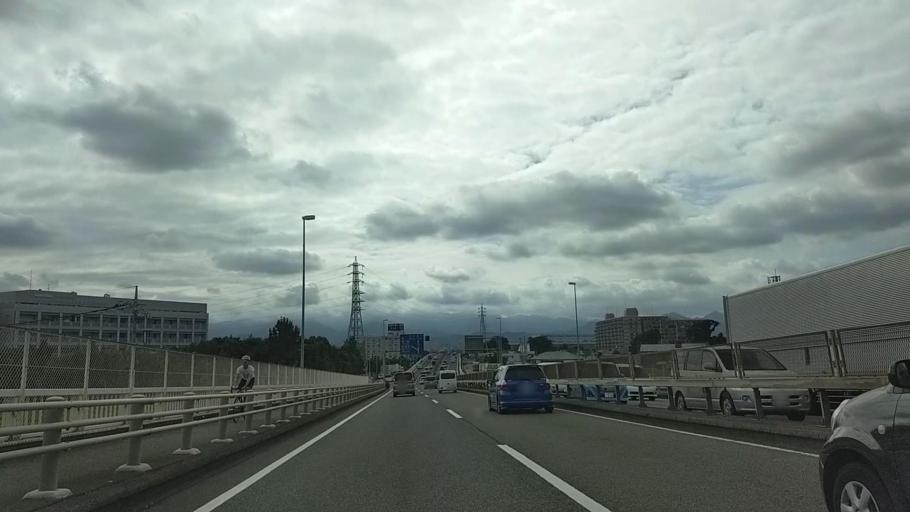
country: JP
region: Kanagawa
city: Zama
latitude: 35.4637
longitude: 139.3941
